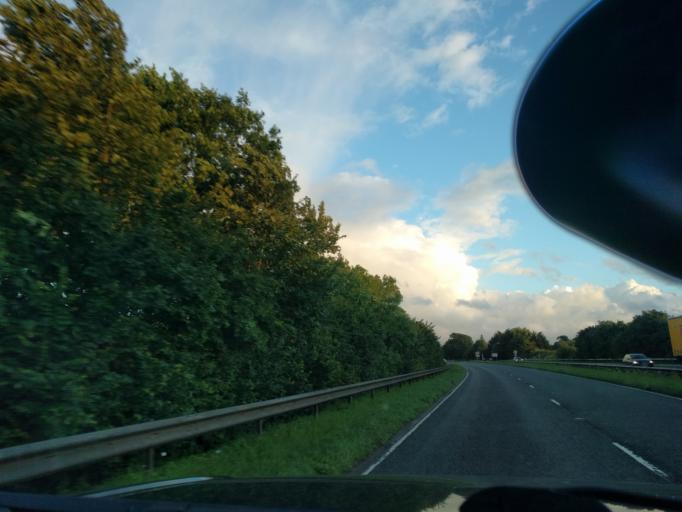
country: GB
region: England
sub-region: Wiltshire
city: Chippenham
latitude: 51.5118
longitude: -2.1236
